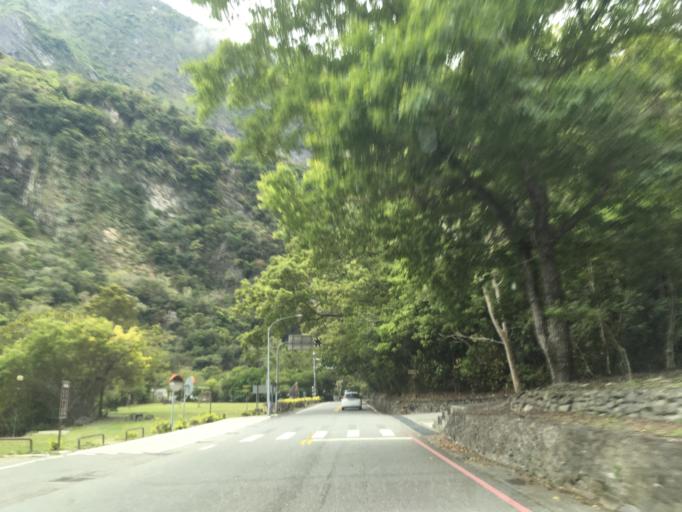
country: TW
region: Taiwan
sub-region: Hualien
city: Hualian
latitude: 24.1787
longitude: 121.5080
